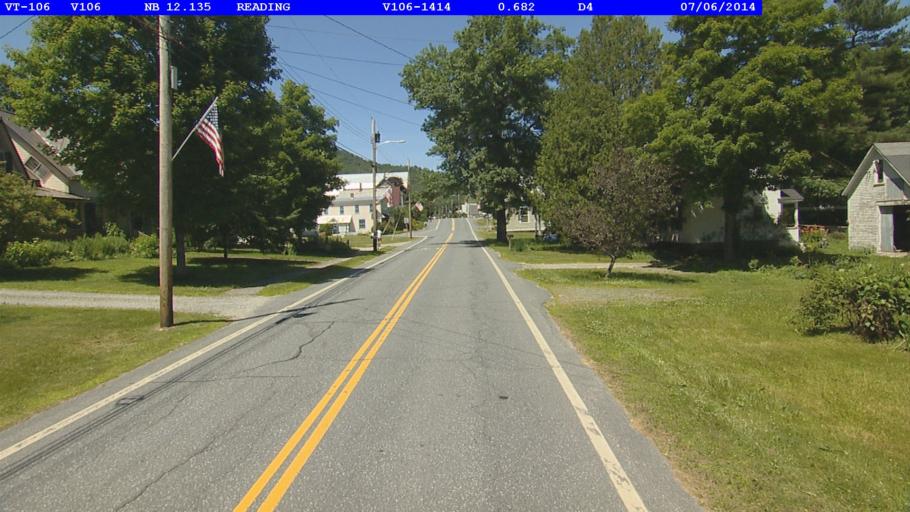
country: US
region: Vermont
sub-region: Windsor County
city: Windsor
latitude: 43.4540
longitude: -72.5373
